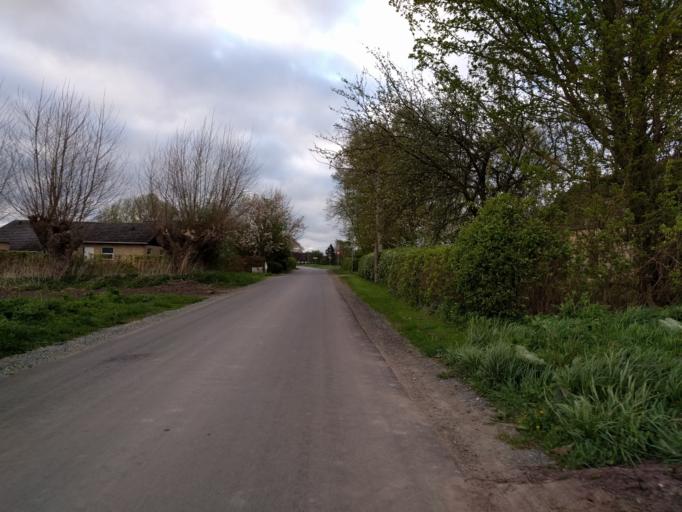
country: DK
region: South Denmark
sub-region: Odense Kommune
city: Bullerup
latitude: 55.4385
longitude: 10.5048
